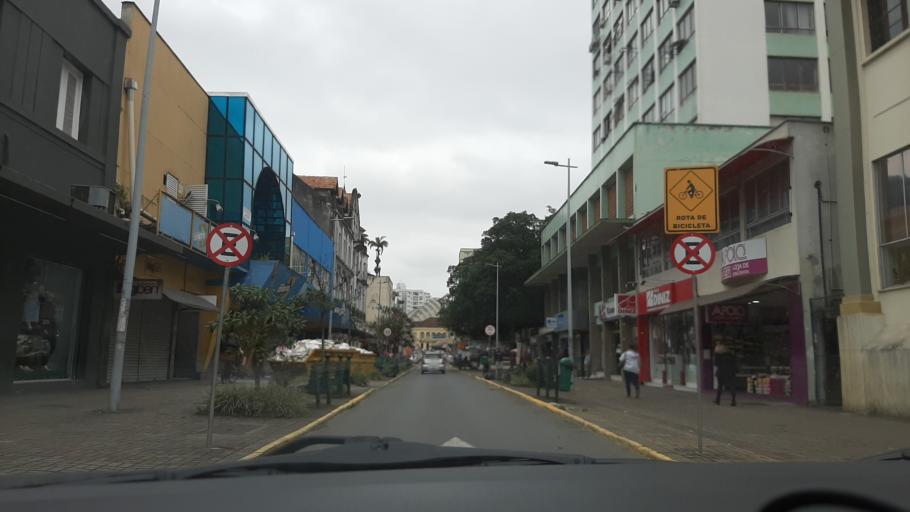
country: BR
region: Santa Catarina
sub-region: Joinville
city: Joinville
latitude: -26.3017
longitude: -48.8455
